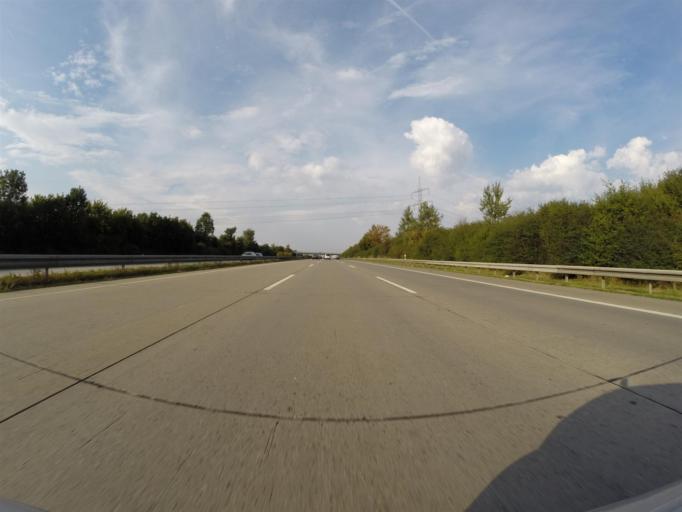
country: DE
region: Thuringia
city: Walpernhain
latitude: 51.0213
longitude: 11.9319
